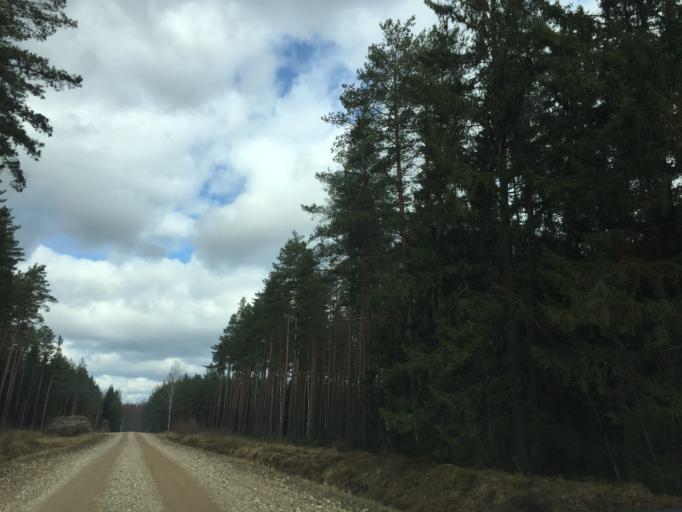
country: LV
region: Vecumnieki
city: Vecumnieki
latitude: 56.5957
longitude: 24.6402
